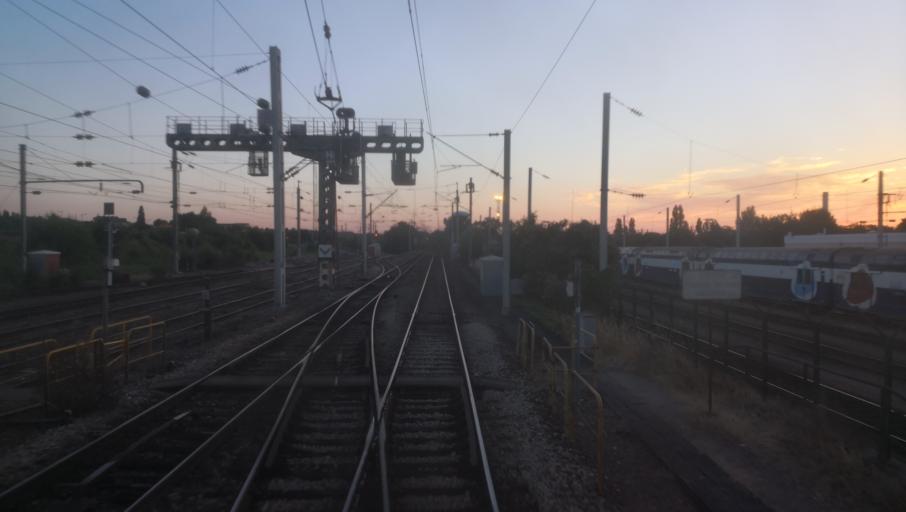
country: FR
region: Ile-de-France
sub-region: Departement des Yvelines
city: Mantes-la-Ville
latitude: 48.9905
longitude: 1.6975
